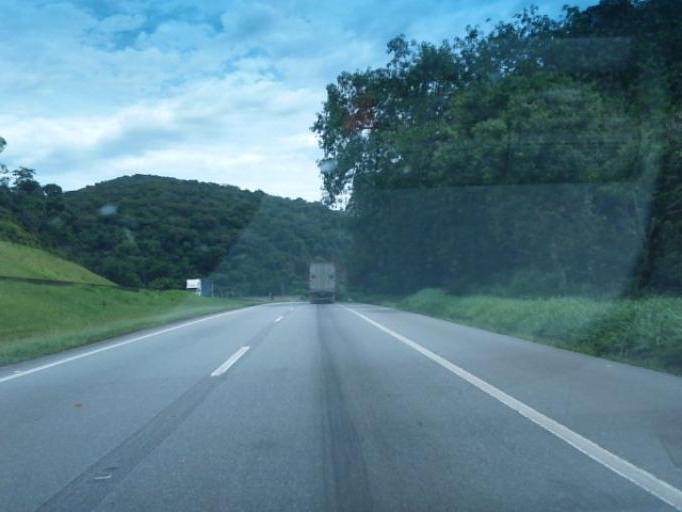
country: BR
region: Sao Paulo
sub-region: Miracatu
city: Miracatu
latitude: -24.1900
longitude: -47.3600
